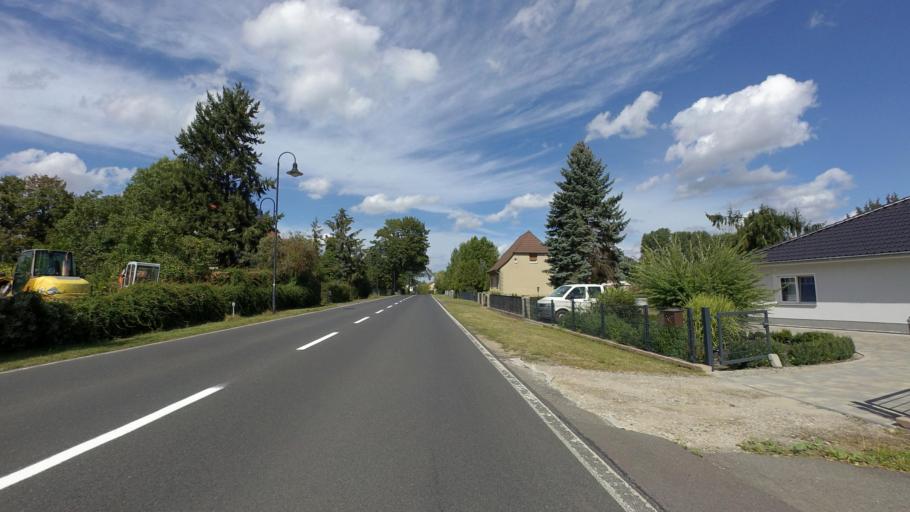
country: DE
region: Brandenburg
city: Wustermark
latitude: 52.5327
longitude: 12.9310
